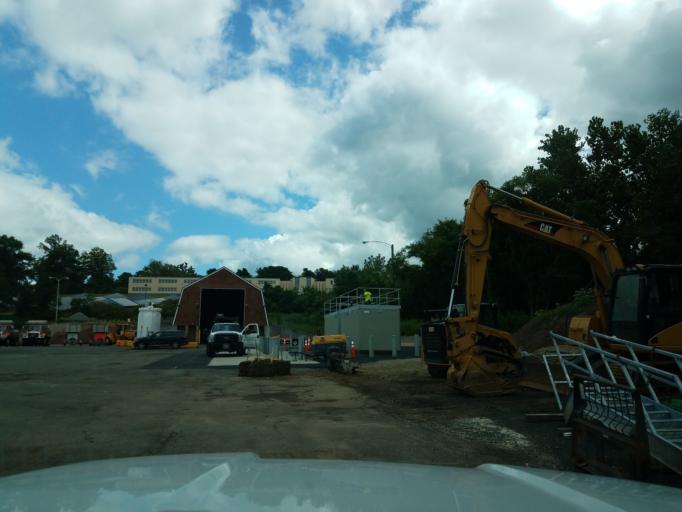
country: US
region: Connecticut
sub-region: Middlesex County
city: Middletown
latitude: 41.5324
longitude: -72.6239
